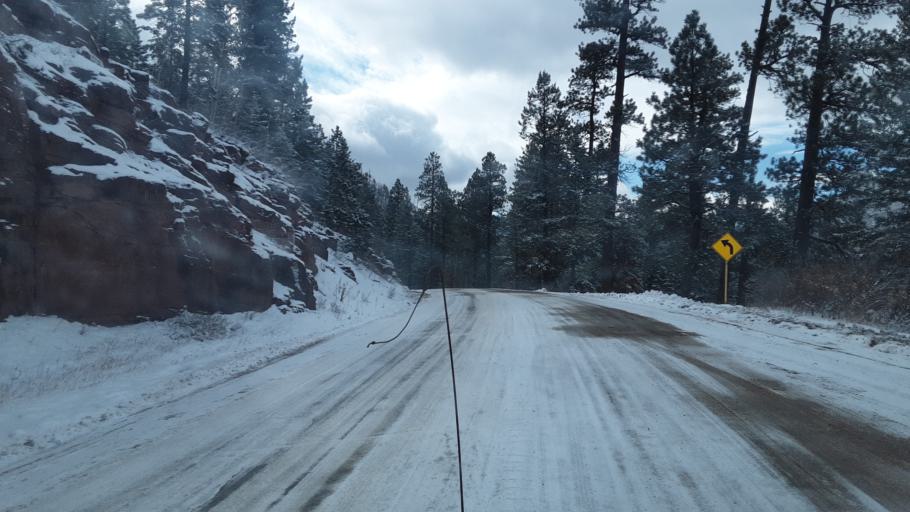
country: US
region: Colorado
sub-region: La Plata County
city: Bayfield
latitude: 37.3809
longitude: -107.6589
